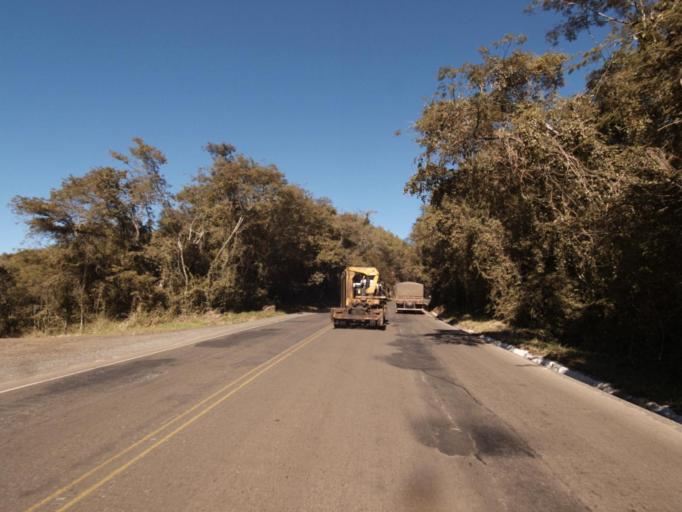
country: BR
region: Santa Catarina
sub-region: Chapeco
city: Chapeco
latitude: -26.9509
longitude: -52.7784
